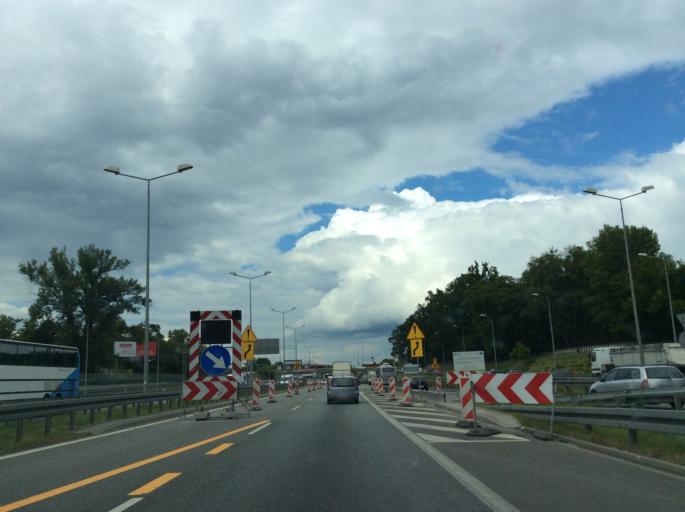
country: PL
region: Masovian Voivodeship
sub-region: Warszawa
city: Bielany
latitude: 52.2594
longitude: 20.9507
